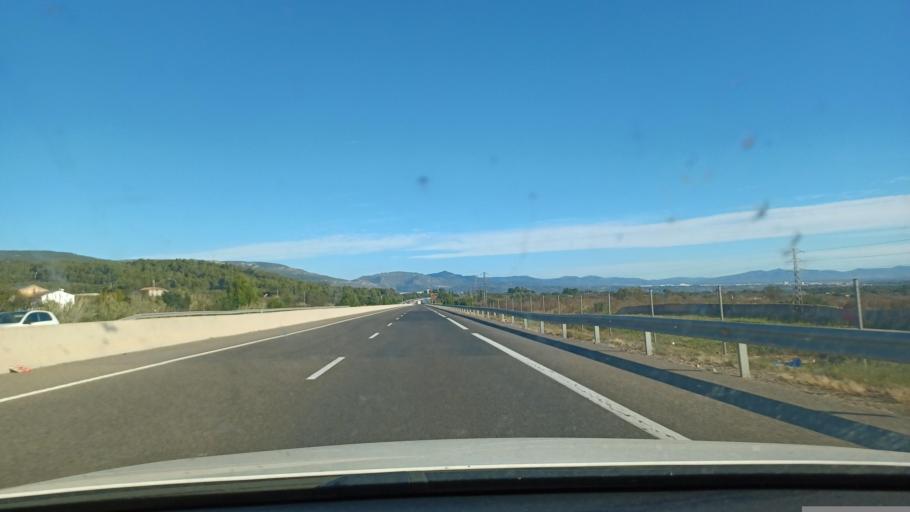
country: ES
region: Catalonia
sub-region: Provincia de Tarragona
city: Alcover
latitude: 41.2335
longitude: 1.1640
